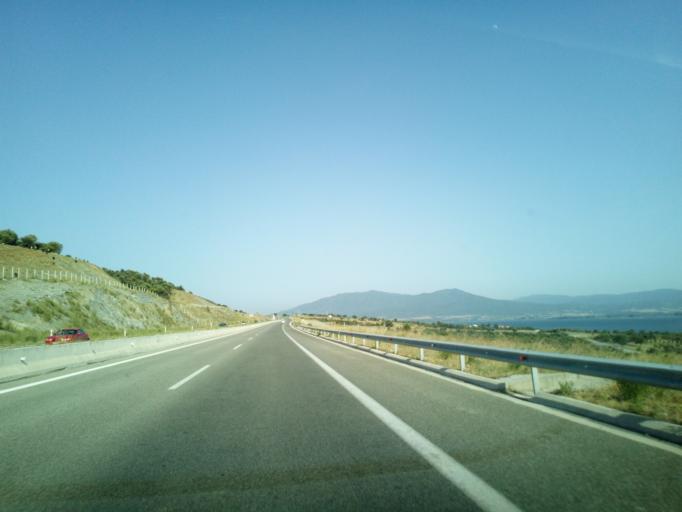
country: GR
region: Central Macedonia
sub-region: Nomos Thessalonikis
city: Nea Apollonia
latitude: 40.6860
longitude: 23.5422
